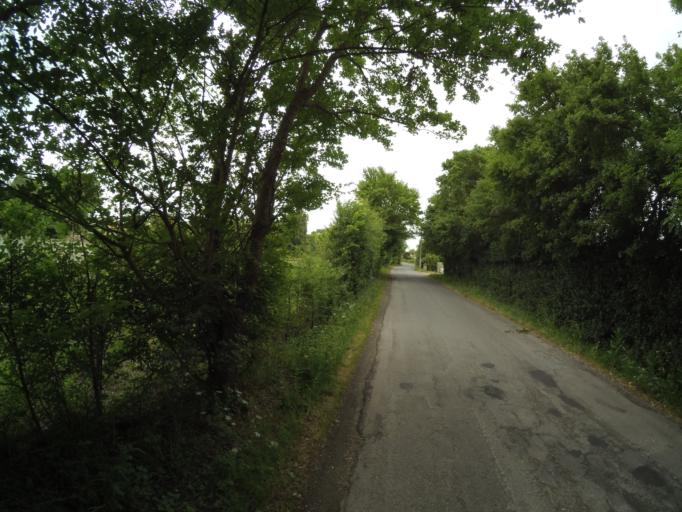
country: FR
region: Poitou-Charentes
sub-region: Departement de la Charente-Maritime
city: Breuil-Magne
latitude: 45.9697
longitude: -0.9811
